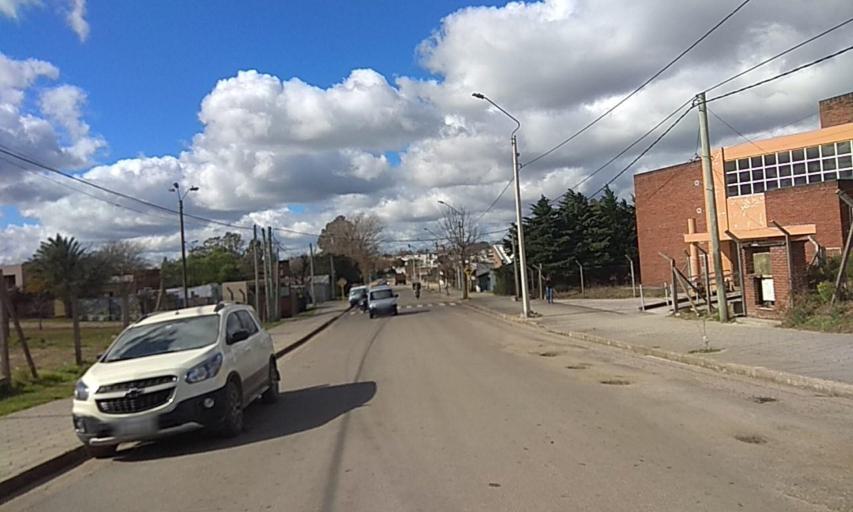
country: UY
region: Florida
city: Florida
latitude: -34.0910
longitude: -56.2264
